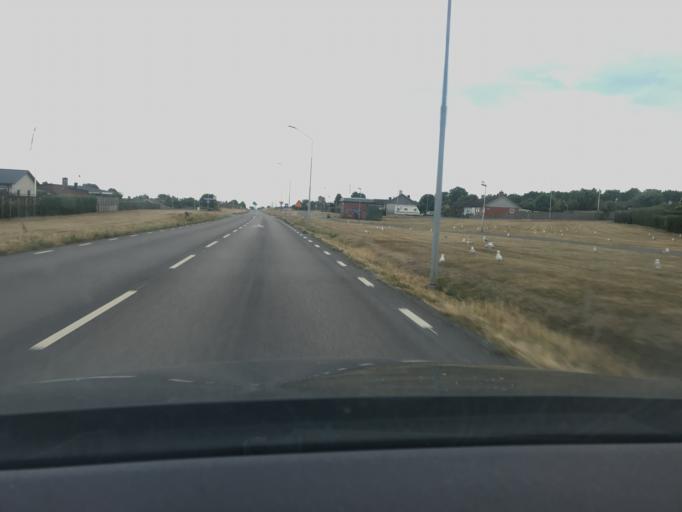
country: SE
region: Skane
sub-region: Simrishamns Kommun
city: Simrishamn
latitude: 55.5467
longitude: 14.3510
